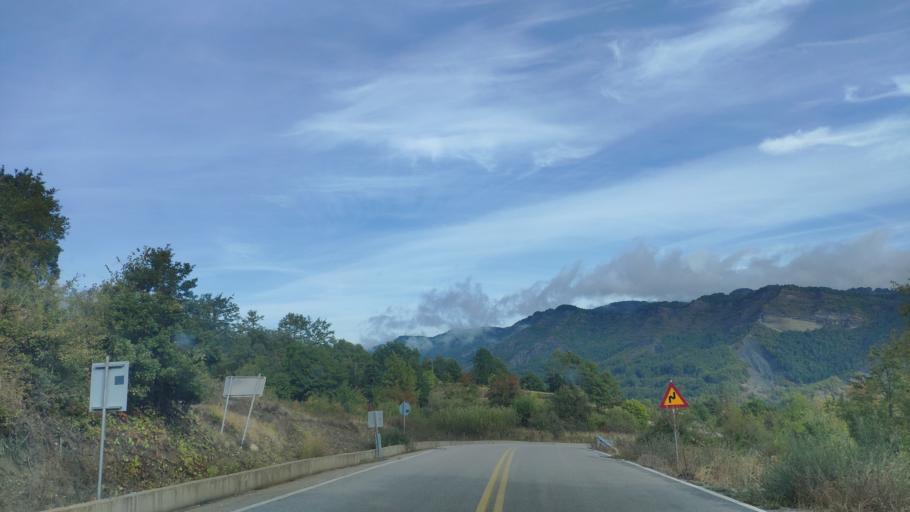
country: GR
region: West Macedonia
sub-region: Nomos Kastorias
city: Nestorio
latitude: 40.2765
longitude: 20.9740
